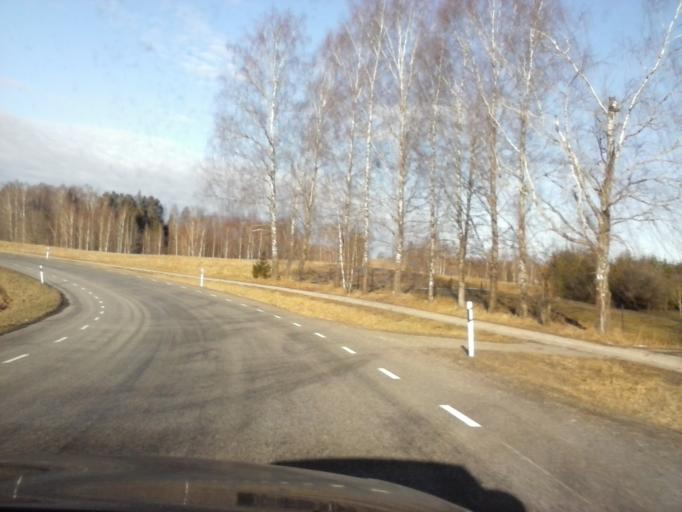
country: EE
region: Tartu
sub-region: Elva linn
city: Elva
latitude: 58.0500
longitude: 26.4465
